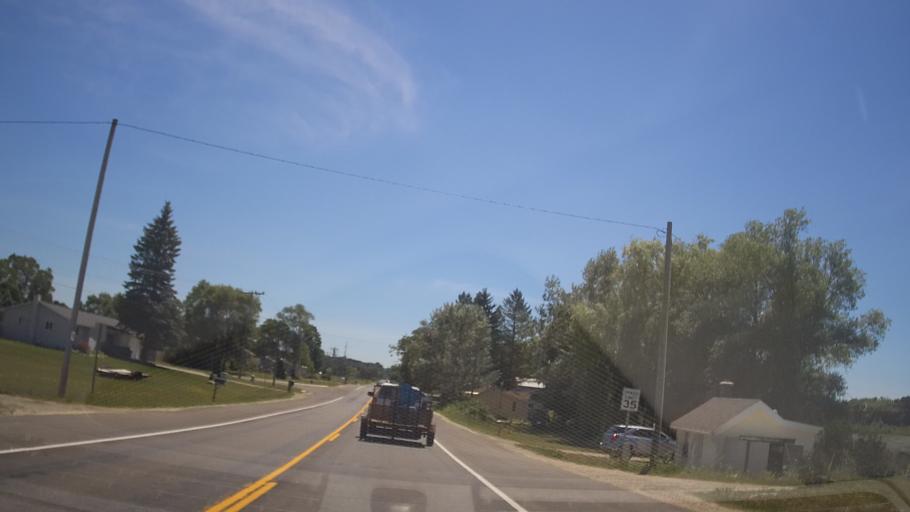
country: US
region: Michigan
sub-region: Grand Traverse County
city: Traverse City
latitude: 44.6600
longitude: -85.6966
